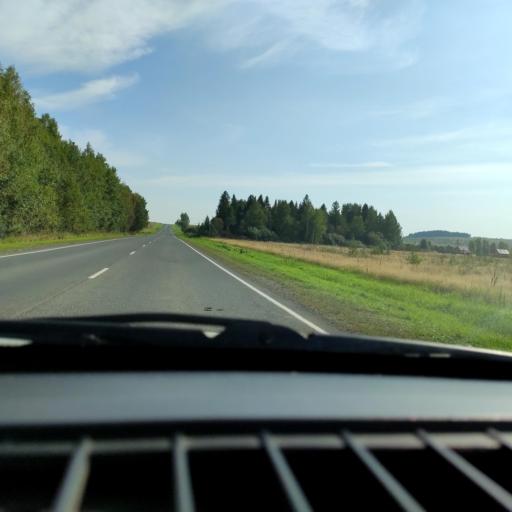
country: RU
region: Perm
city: Ust'-Kachka
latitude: 57.9614
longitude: 55.7298
